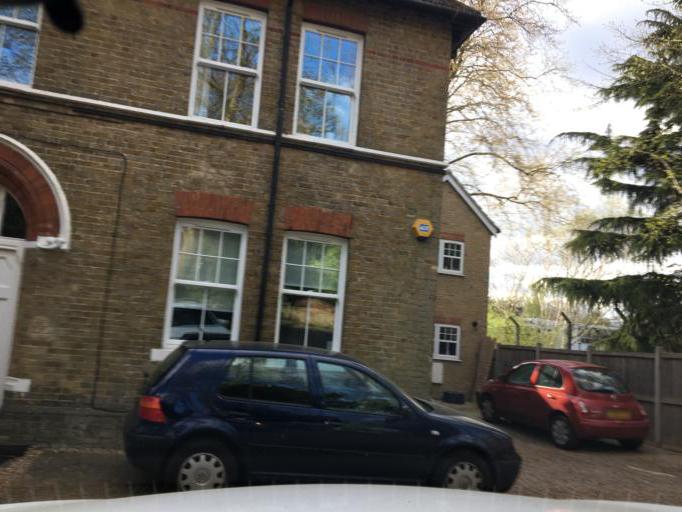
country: GB
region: England
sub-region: Greater London
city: Chislehurst
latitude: 51.4440
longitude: 0.0518
